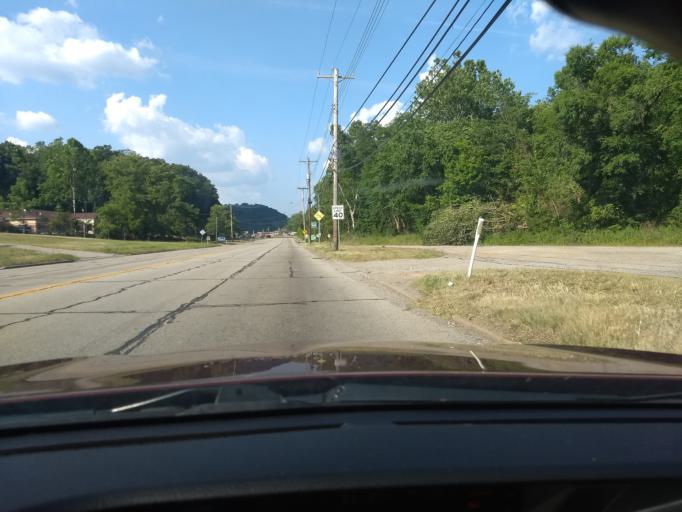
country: US
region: Pennsylvania
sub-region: Allegheny County
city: White Oak
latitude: 40.3288
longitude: -79.8169
